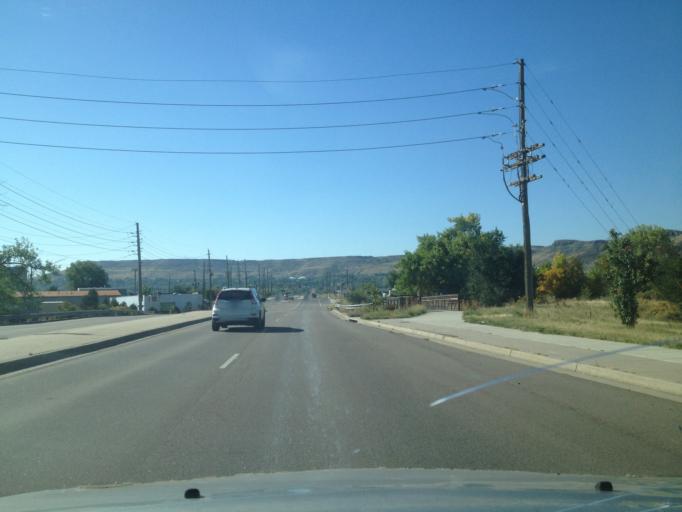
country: US
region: Colorado
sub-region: Jefferson County
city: Applewood
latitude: 39.7786
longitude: -105.1749
